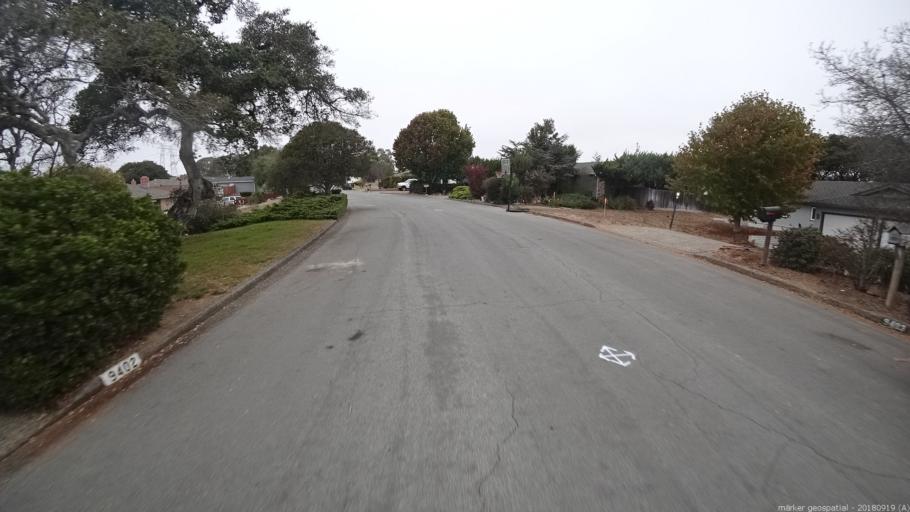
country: US
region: California
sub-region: Monterey County
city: Castroville
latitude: 36.7811
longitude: -121.7154
